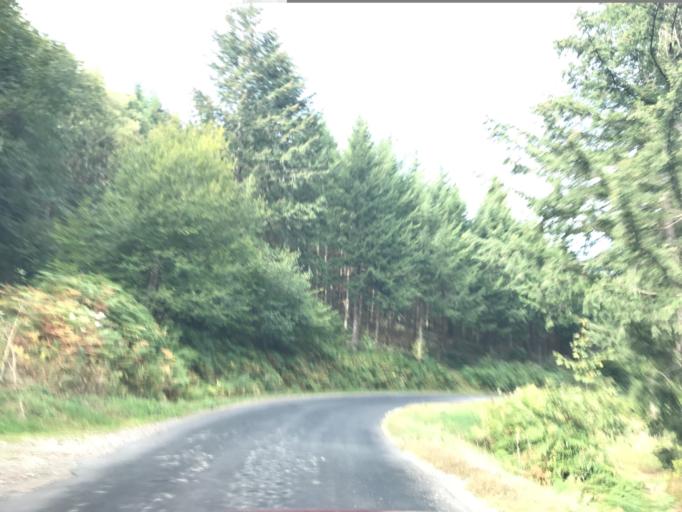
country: FR
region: Auvergne
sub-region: Departement du Puy-de-Dome
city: Celles-sur-Durolle
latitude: 45.8257
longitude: 3.6555
